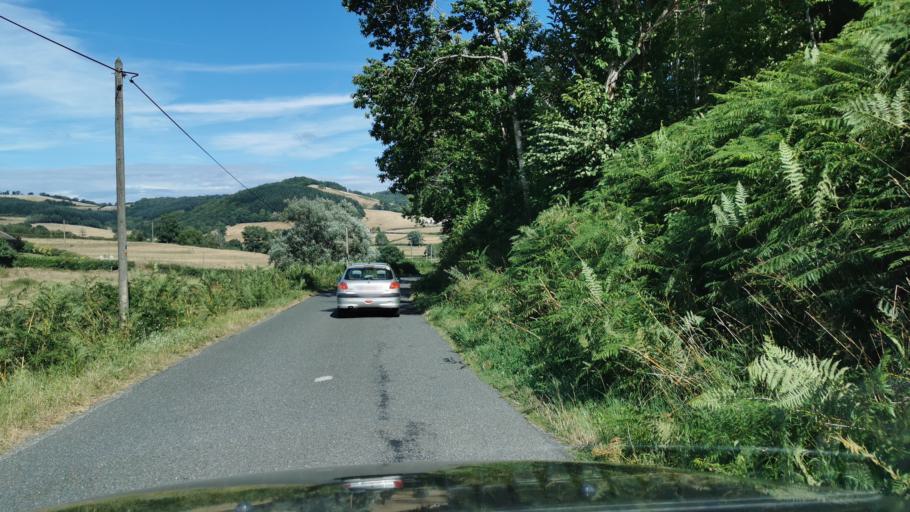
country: FR
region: Bourgogne
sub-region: Departement de Saone-et-Loire
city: Marmagne
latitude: 46.8065
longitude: 4.3207
